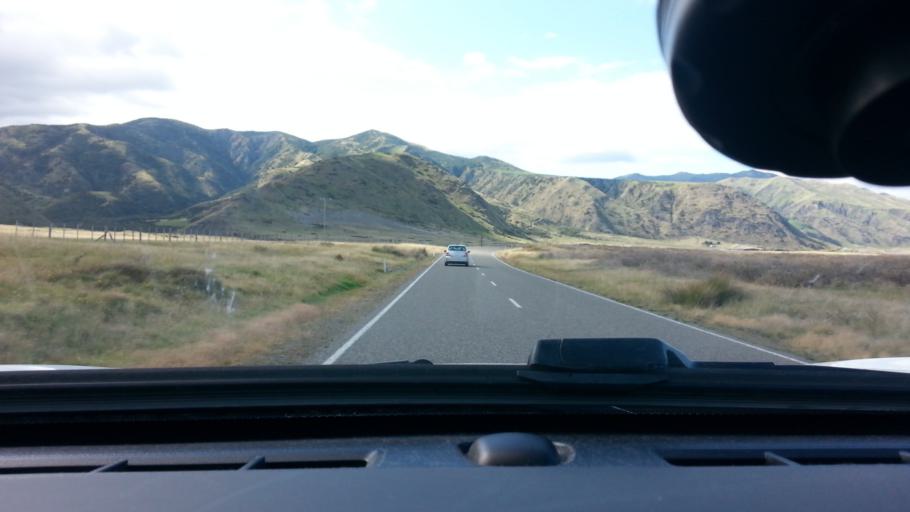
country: NZ
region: Wellington
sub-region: South Wairarapa District
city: Waipawa
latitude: -41.5291
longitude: 175.2040
